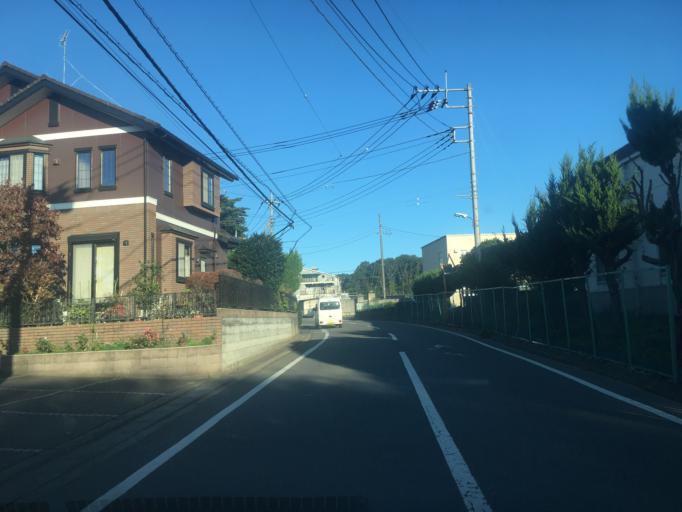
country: JP
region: Saitama
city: Sayama
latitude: 35.8038
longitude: 139.3827
